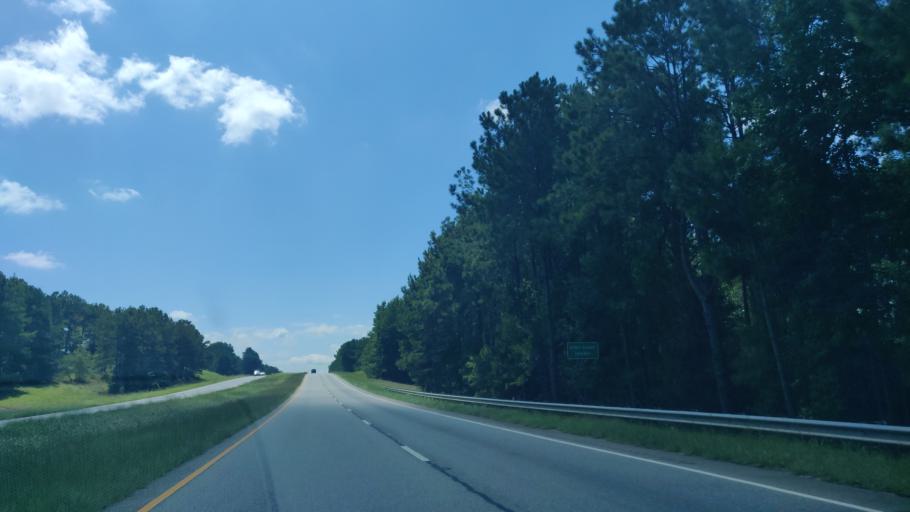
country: US
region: Georgia
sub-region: Chattahoochee County
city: Cusseta
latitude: 32.2952
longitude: -84.7730
